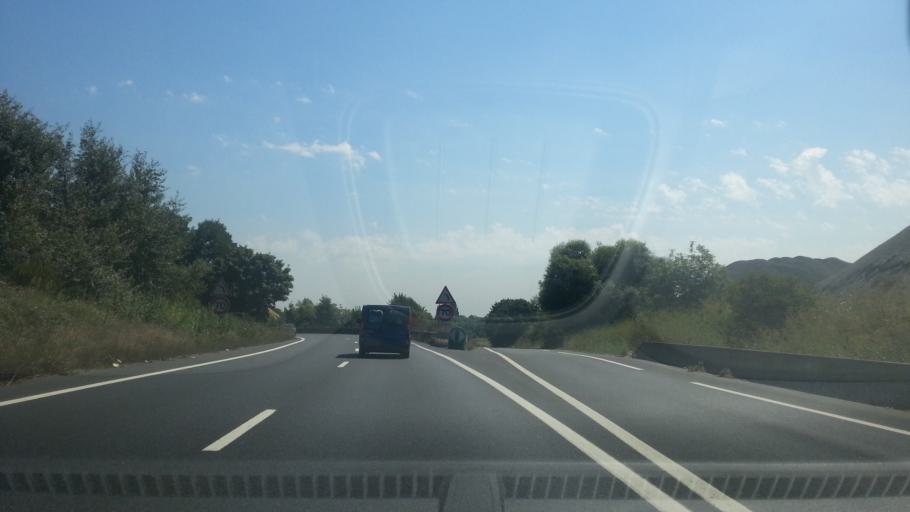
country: FR
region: Ile-de-France
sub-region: Departement de l'Essonne
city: Champlan
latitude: 48.7115
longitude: 2.2856
